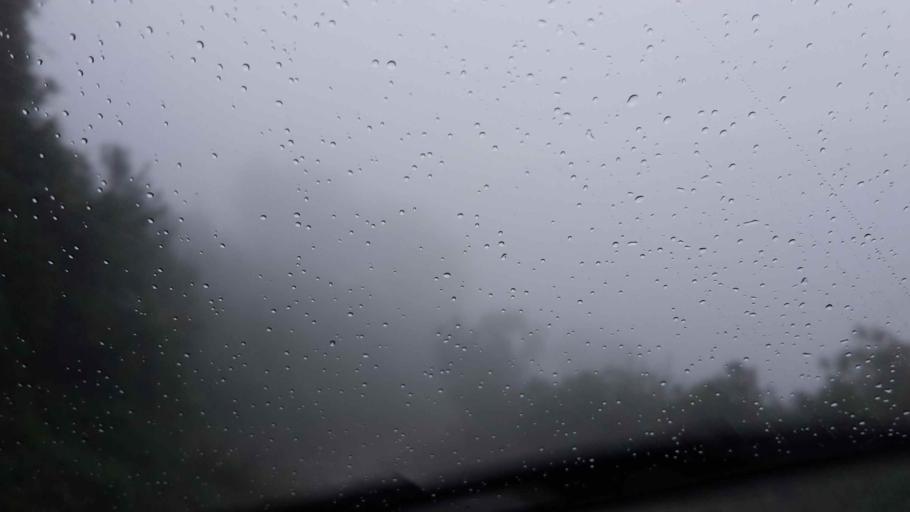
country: BO
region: Cochabamba
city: Colomi
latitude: -17.0922
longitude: -65.9831
